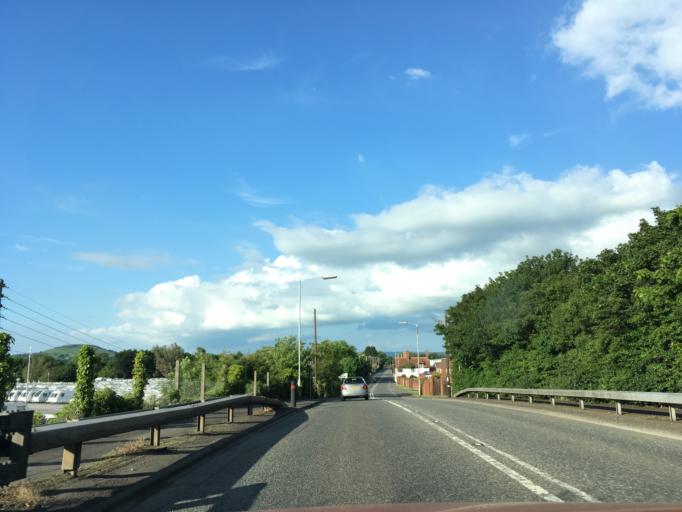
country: GB
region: England
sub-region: Somerset
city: Highbridge
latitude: 51.2250
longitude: -2.9710
